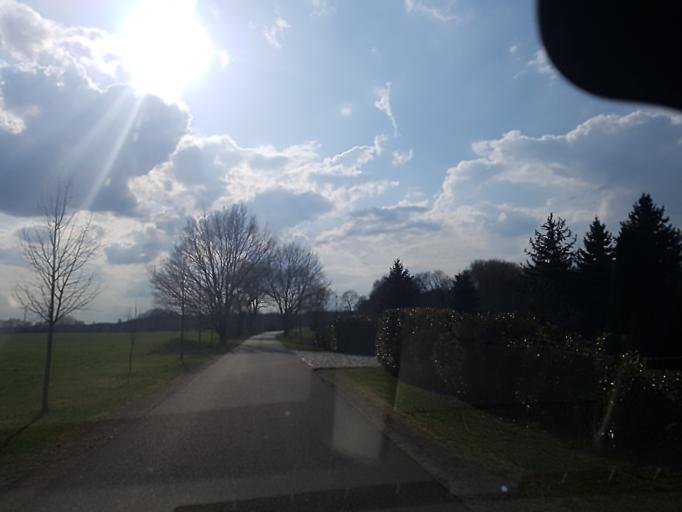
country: DE
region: Brandenburg
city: Doberlug-Kirchhain
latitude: 51.6105
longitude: 13.5386
